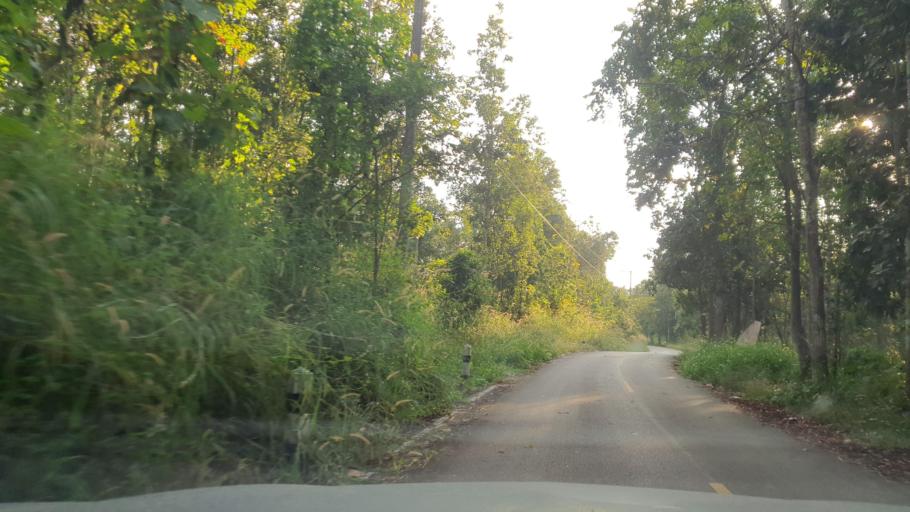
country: TH
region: Chiang Mai
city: Mae On
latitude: 18.8712
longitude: 99.2465
